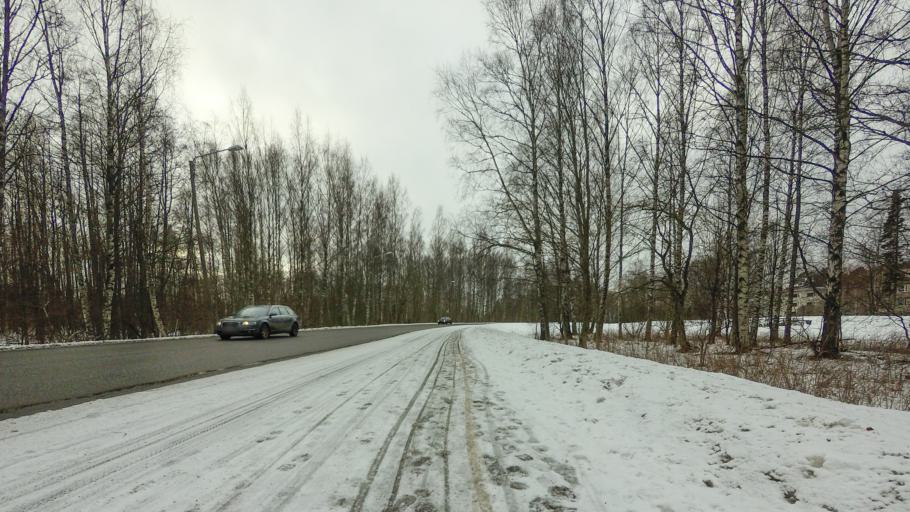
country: FI
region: Uusimaa
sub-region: Helsinki
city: Vantaa
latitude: 60.1953
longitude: 25.0615
